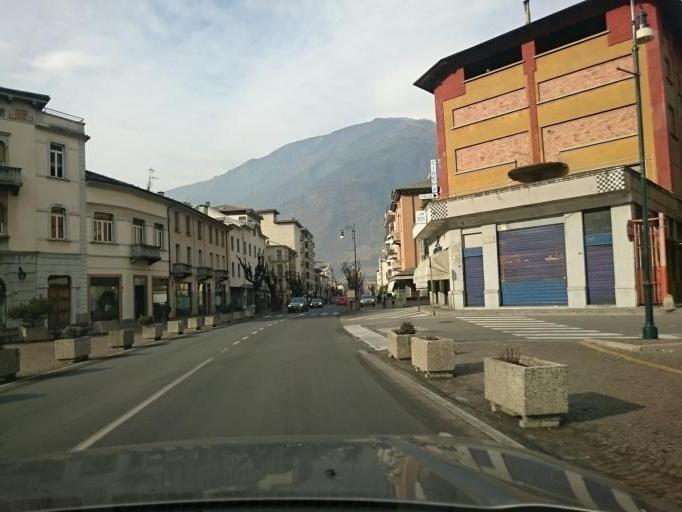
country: IT
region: Lombardy
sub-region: Provincia di Sondrio
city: Tirano
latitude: 46.2162
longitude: 10.1705
